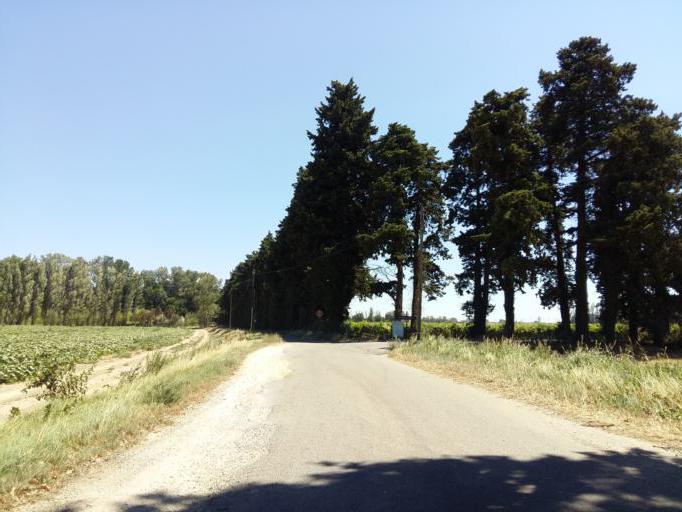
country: FR
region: Provence-Alpes-Cote d'Azur
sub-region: Departement du Vaucluse
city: Mornas
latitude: 44.1773
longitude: 4.7270
